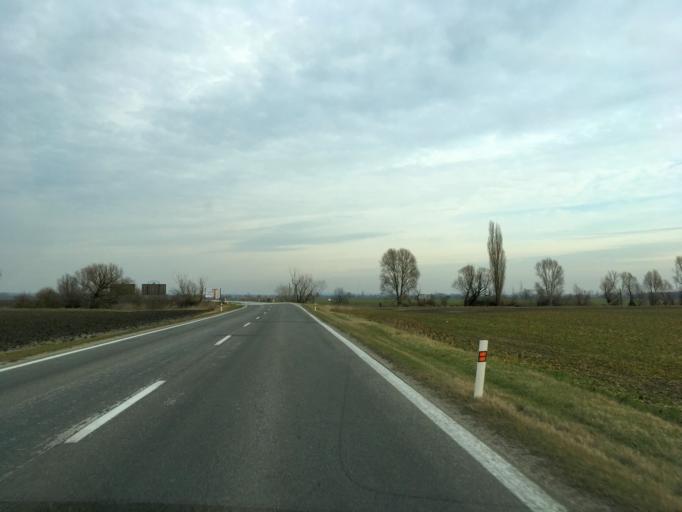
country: SK
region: Nitriansky
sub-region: Okres Nove Zamky
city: Nove Zamky
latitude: 47.9916
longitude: 18.2252
